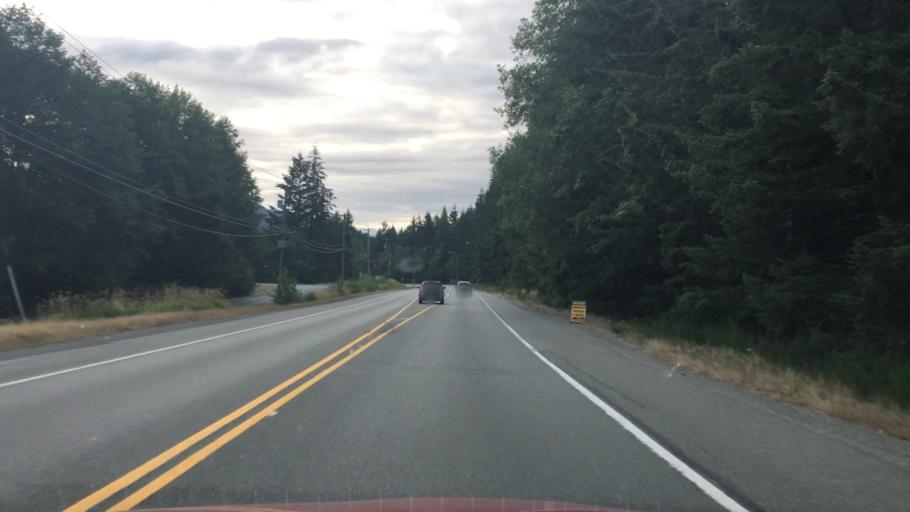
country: CA
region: British Columbia
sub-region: Regional District of Nanaimo
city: Parksville
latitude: 49.3119
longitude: -124.5067
